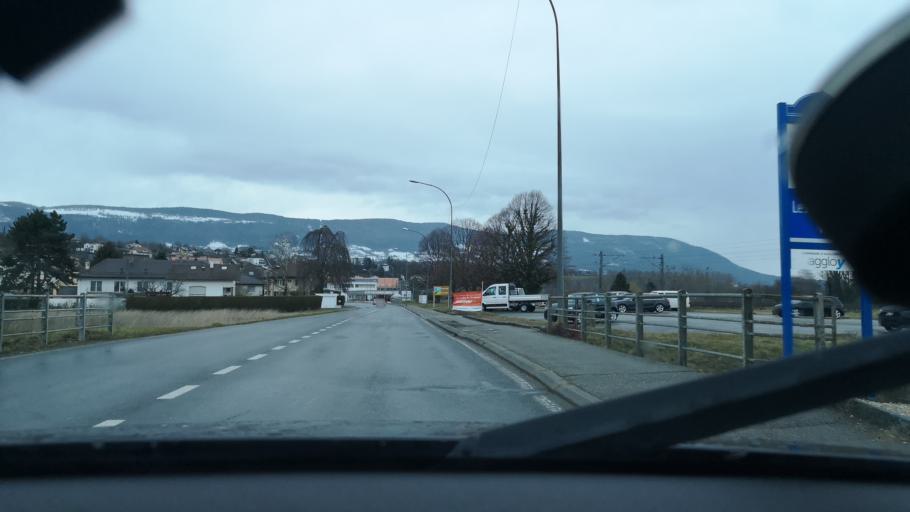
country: CH
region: Vaud
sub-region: Jura-Nord vaudois District
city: Montagny
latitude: 46.7943
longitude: 6.6281
